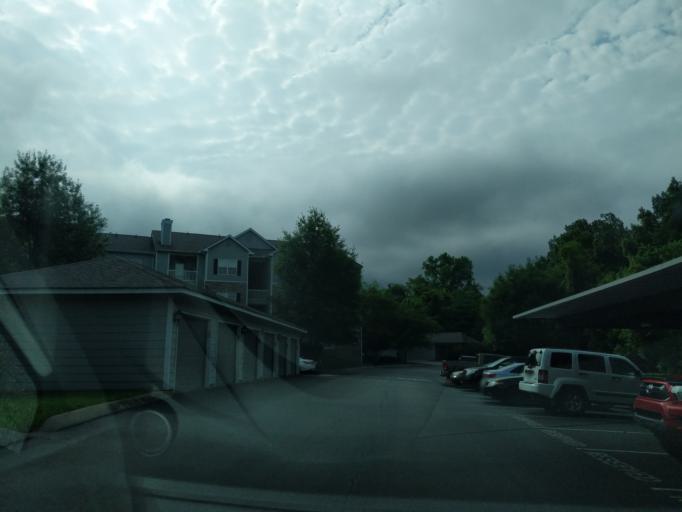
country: US
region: Tennessee
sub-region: Davidson County
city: Lakewood
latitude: 36.1732
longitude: -86.6080
